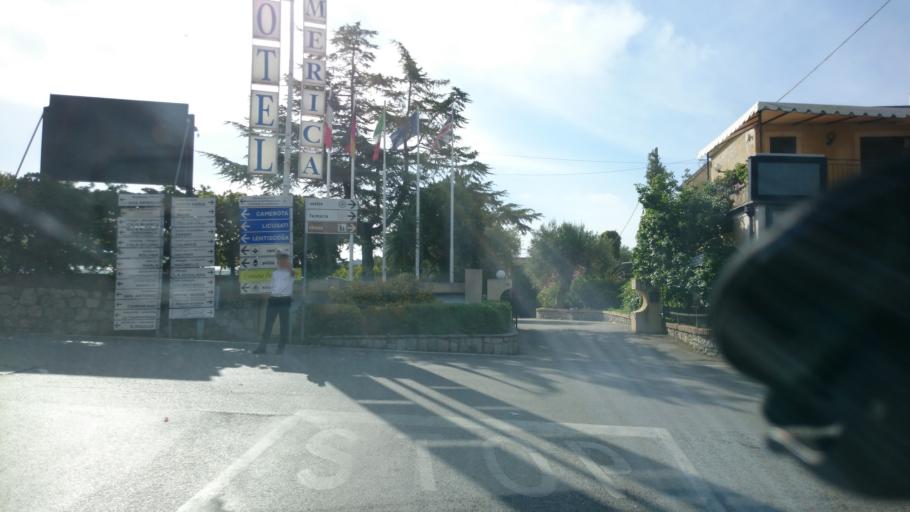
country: IT
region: Campania
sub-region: Provincia di Salerno
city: Marina di Camerota
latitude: 40.0030
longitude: 15.3709
